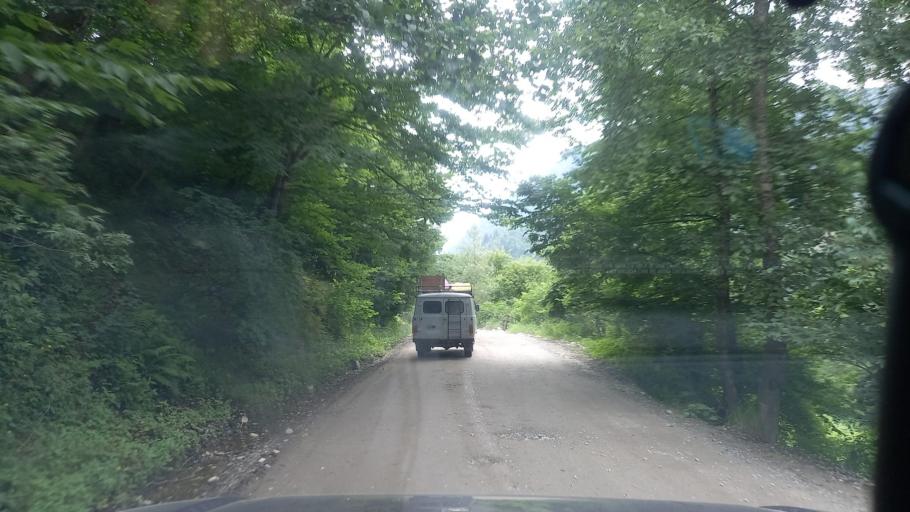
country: RU
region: Karachayevo-Cherkesiya
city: Kurdzhinovo
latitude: 43.8172
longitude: 40.9151
